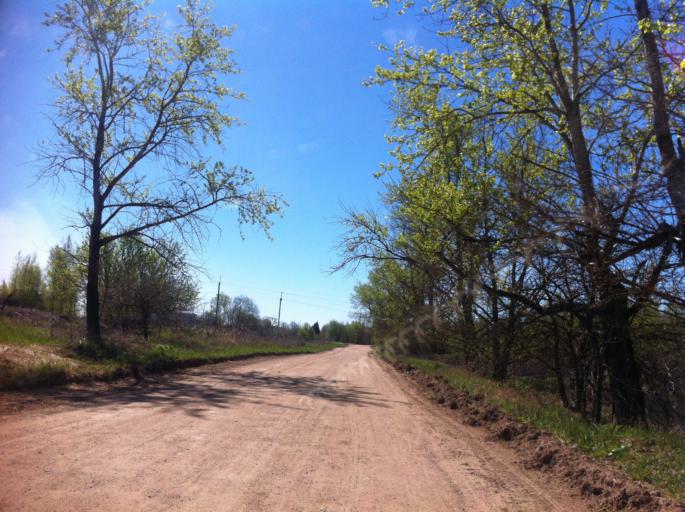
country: RU
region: Pskov
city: Izborsk
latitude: 57.7900
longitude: 27.9631
